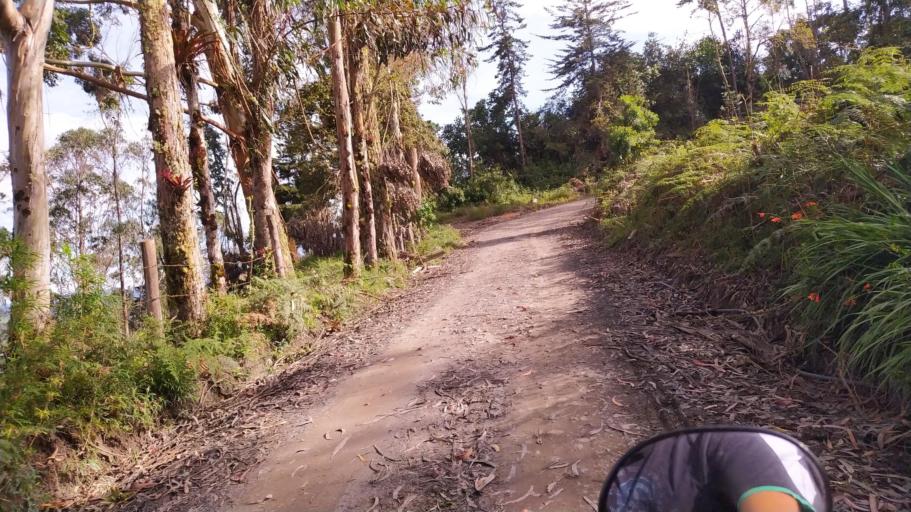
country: CO
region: Cundinamarca
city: Tenza
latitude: 5.0898
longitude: -73.4771
